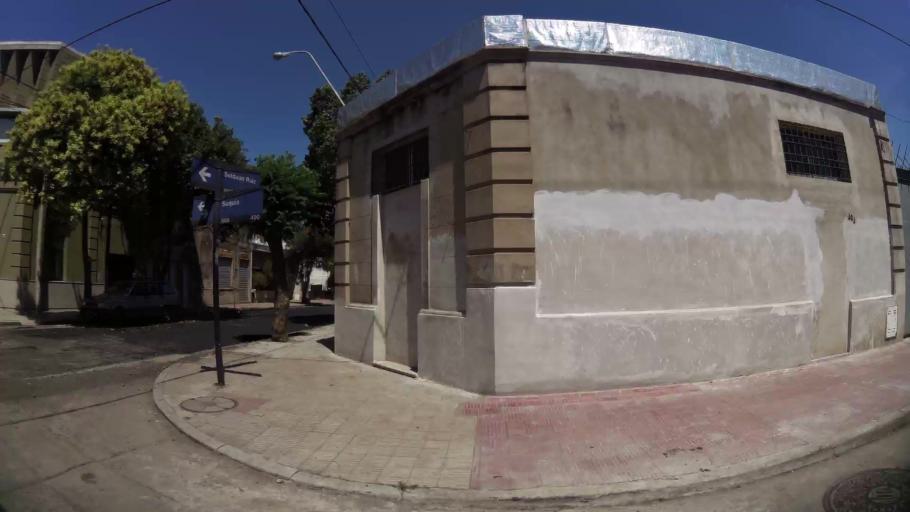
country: AR
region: Cordoba
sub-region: Departamento de Capital
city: Cordoba
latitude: -31.3884
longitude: -64.1981
